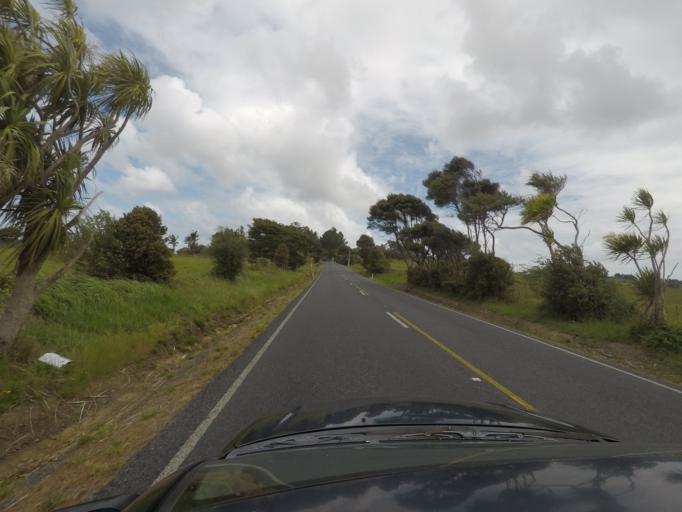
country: NZ
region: Auckland
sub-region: Auckland
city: Parakai
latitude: -36.6359
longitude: 174.5055
